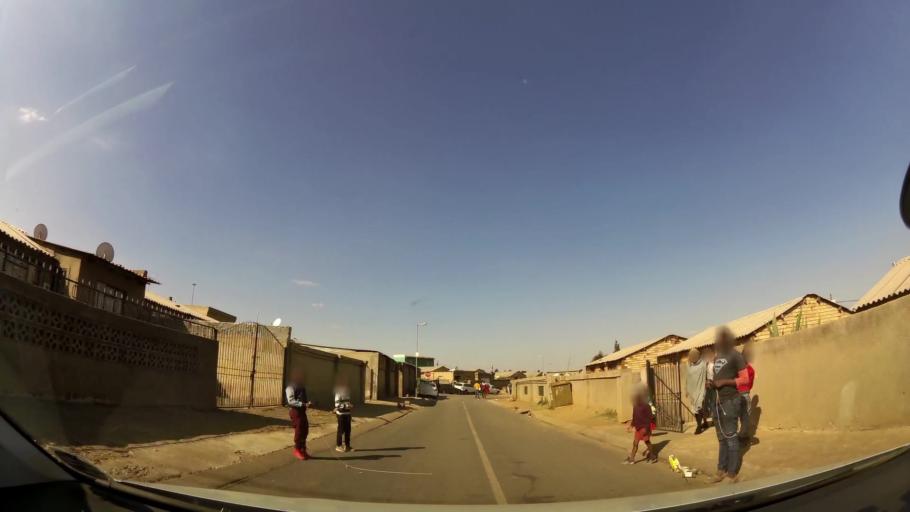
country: ZA
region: Gauteng
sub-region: City of Johannesburg Metropolitan Municipality
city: Soweto
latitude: -26.2839
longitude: 27.8619
